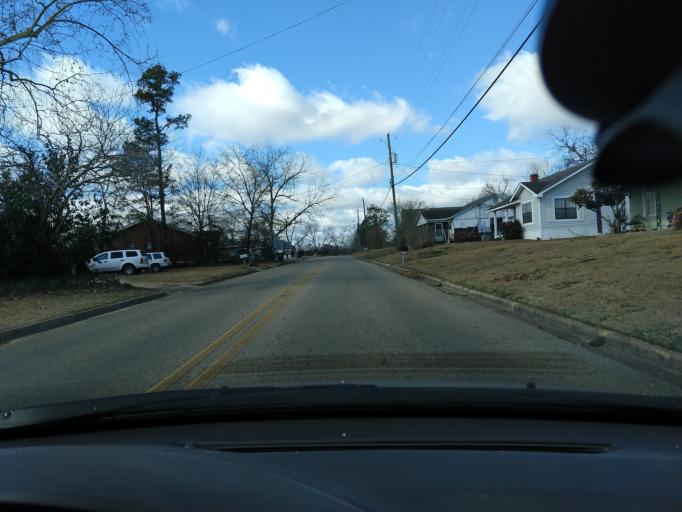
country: US
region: Alabama
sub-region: Coffee County
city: Enterprise
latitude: 31.3205
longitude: -85.8607
